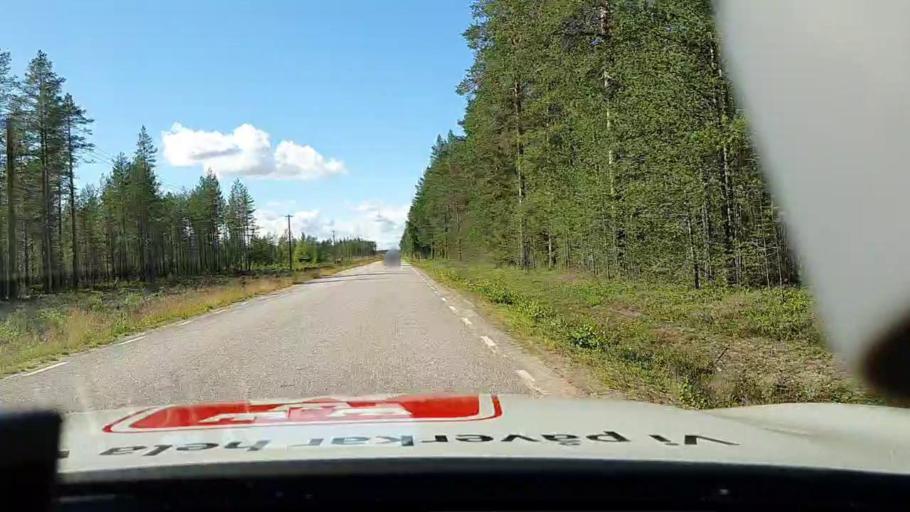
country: SE
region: Norrbotten
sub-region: Overkalix Kommun
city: OEverkalix
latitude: 66.2520
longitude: 22.8750
